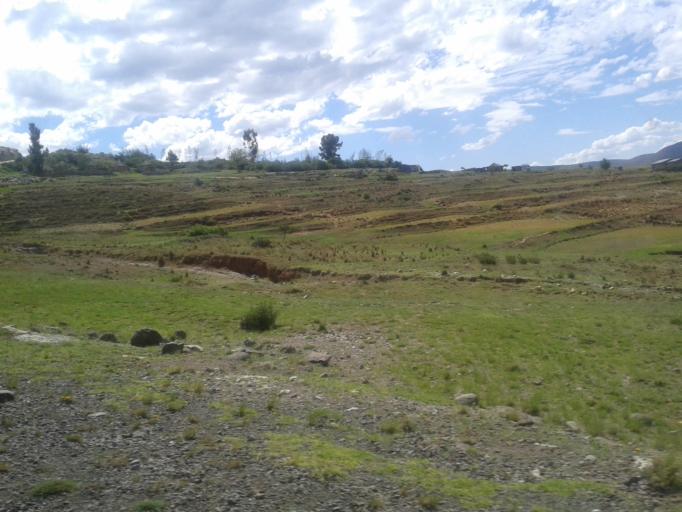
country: LS
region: Qacha's Nek
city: Qacha's Nek
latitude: -30.0331
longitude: 28.3163
